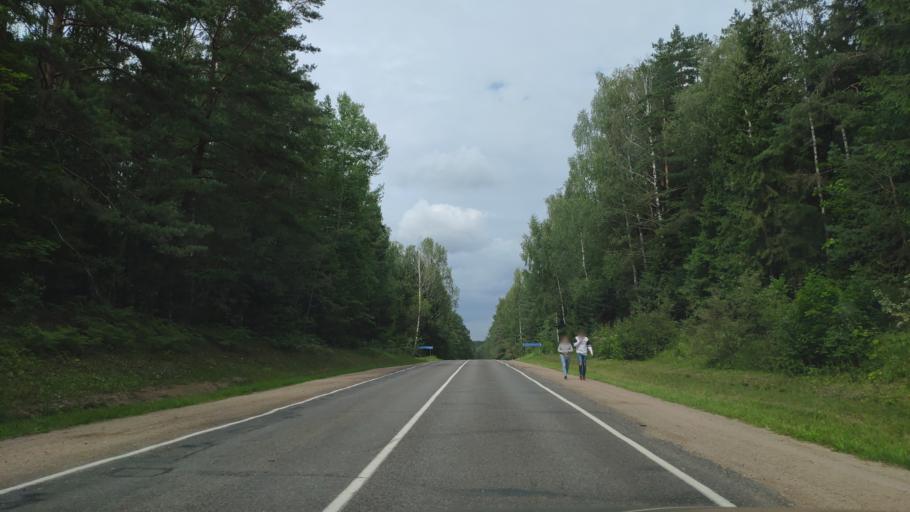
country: BY
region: Minsk
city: Novosel'ye
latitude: 53.9434
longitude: 27.2449
